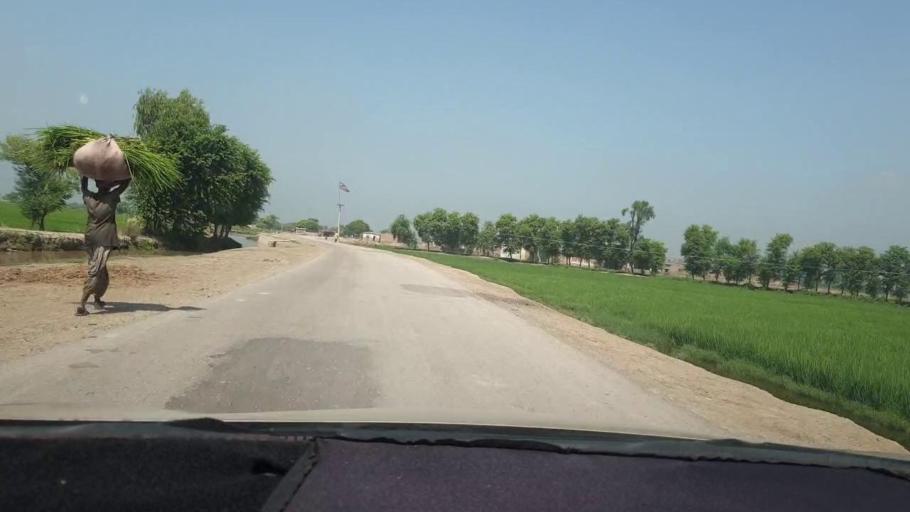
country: PK
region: Sindh
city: Miro Khan
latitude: 27.7704
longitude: 68.0640
